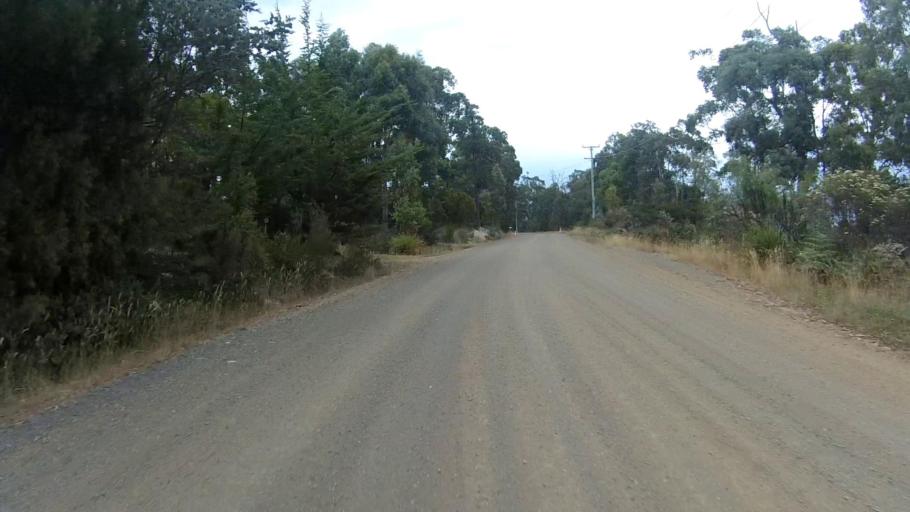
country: AU
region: Tasmania
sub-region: Huon Valley
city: Cygnet
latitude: -43.2257
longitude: 147.0974
